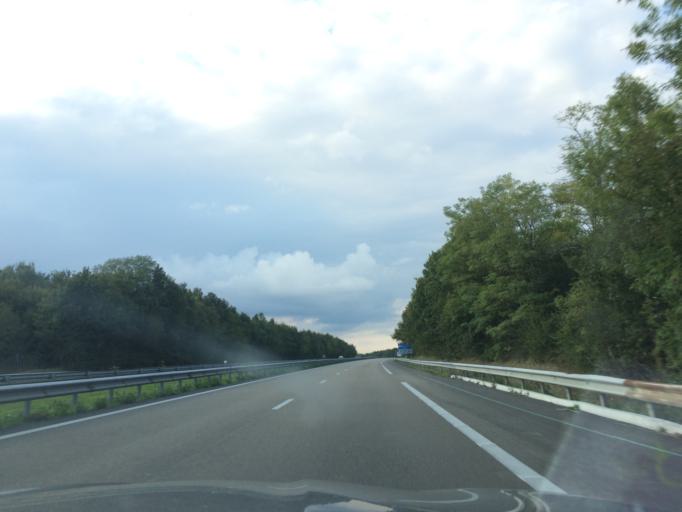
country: FR
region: Ile-de-France
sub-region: Departement de Seine-et-Marne
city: Egreville
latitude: 48.1410
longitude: 2.9129
